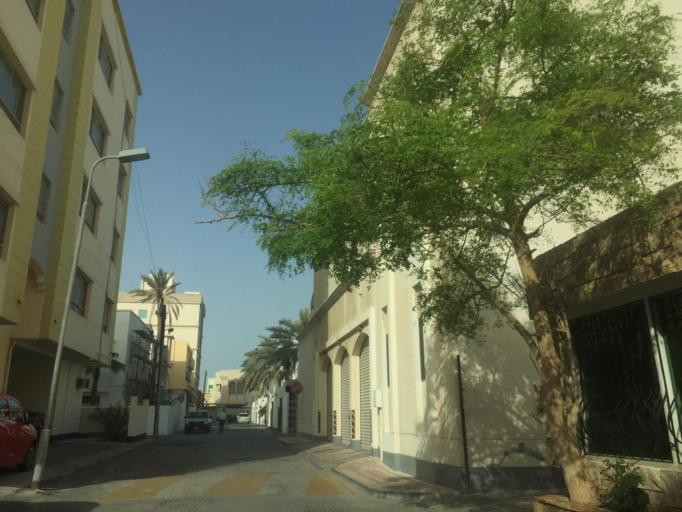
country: BH
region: Manama
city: Manama
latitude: 26.2208
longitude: 50.5812
